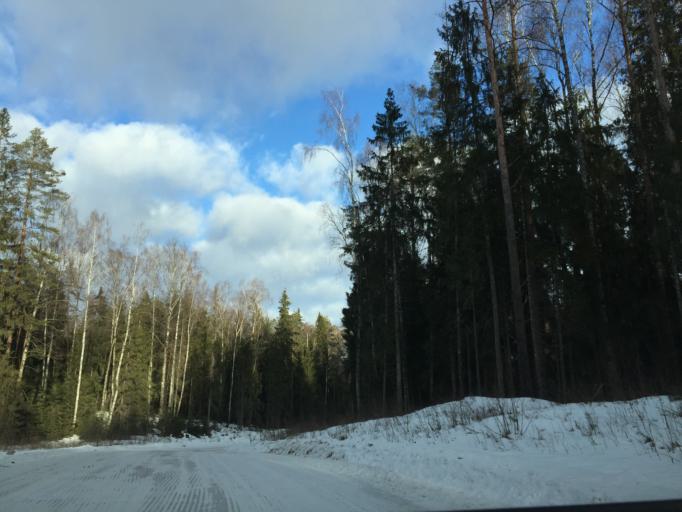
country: LV
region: Ogre
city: Jumprava
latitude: 56.5981
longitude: 24.9953
